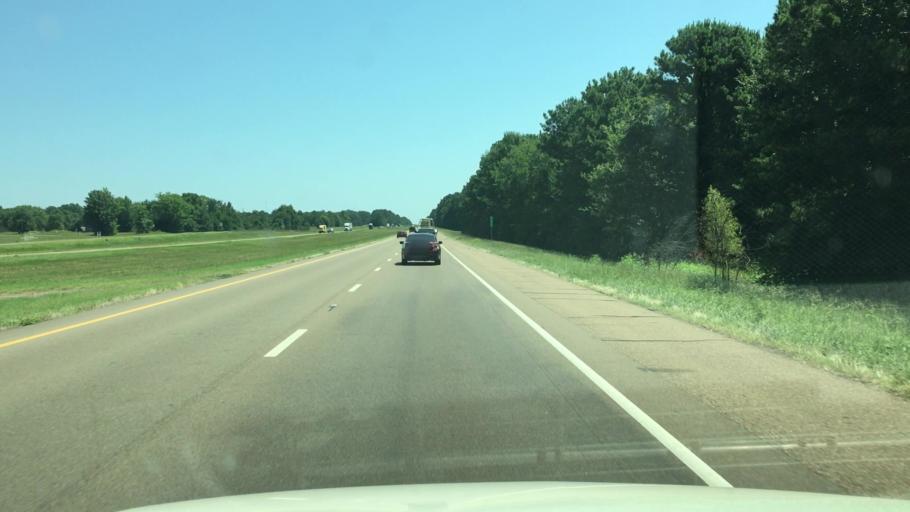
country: US
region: Texas
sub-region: Bowie County
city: New Boston
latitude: 33.4493
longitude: -94.5047
